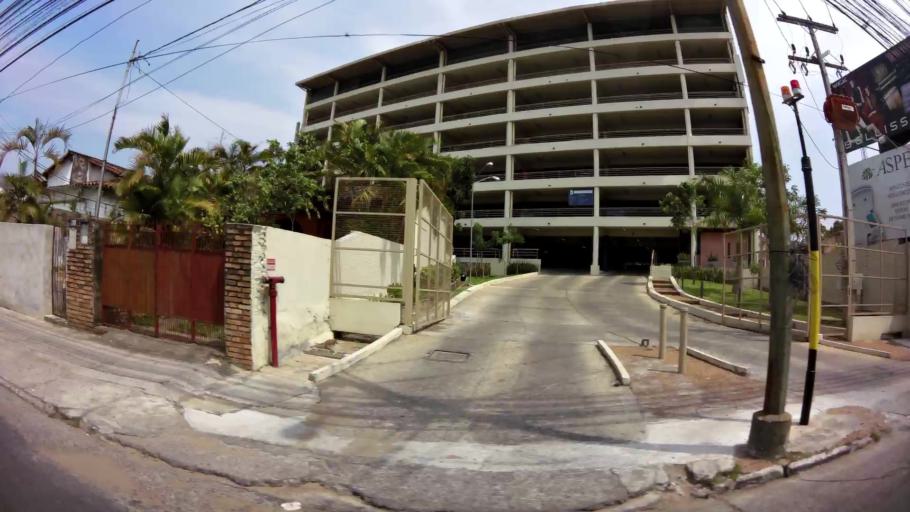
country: PY
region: Asuncion
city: Asuncion
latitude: -25.2873
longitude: -57.5958
